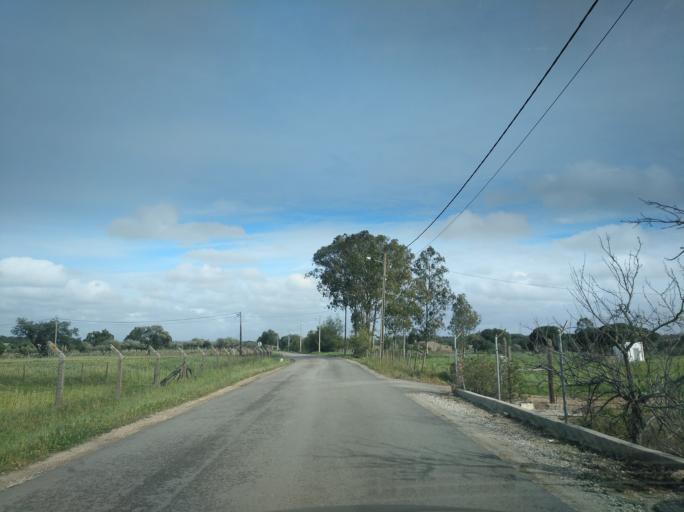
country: PT
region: Setubal
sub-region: Grandola
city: Grandola
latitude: 38.1877
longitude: -8.5616
